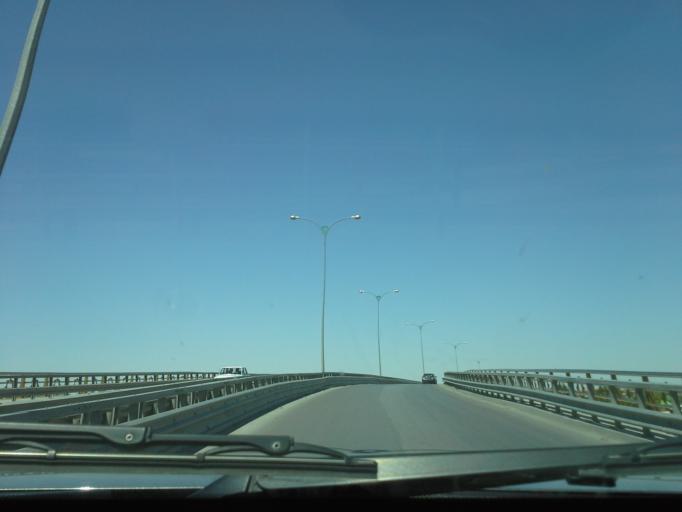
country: TM
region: Balkan
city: Serdar
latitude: 38.9783
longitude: 56.2778
